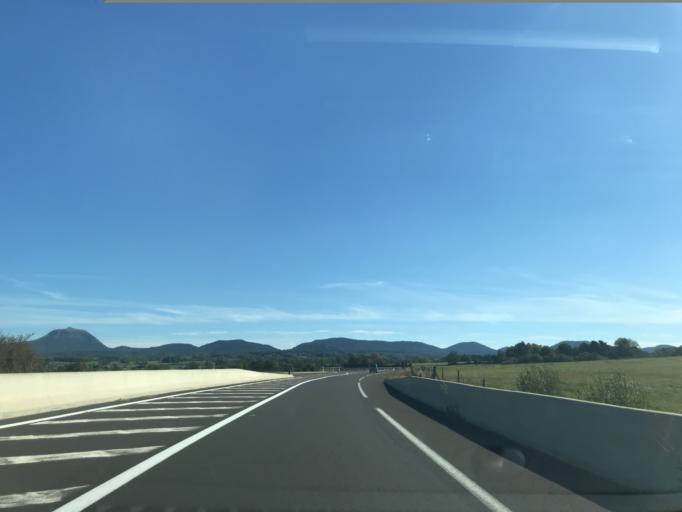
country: FR
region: Auvergne
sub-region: Departement du Puy-de-Dome
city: Gelles
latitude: 45.7381
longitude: 2.8458
